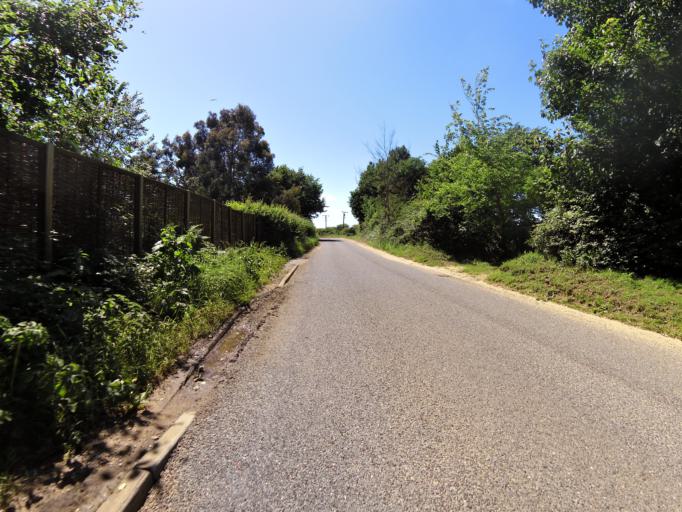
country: GB
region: England
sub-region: Suffolk
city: Felixstowe
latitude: 52.0423
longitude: 1.4181
